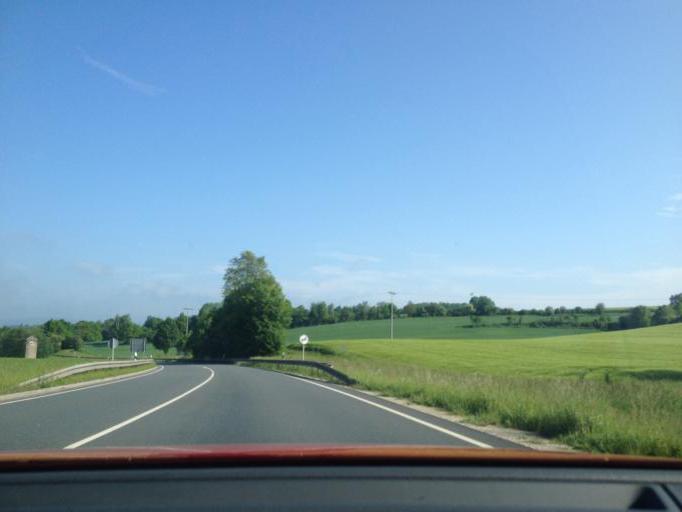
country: DE
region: Bavaria
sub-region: Upper Palatinate
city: Kastl
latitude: 49.8350
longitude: 11.8927
